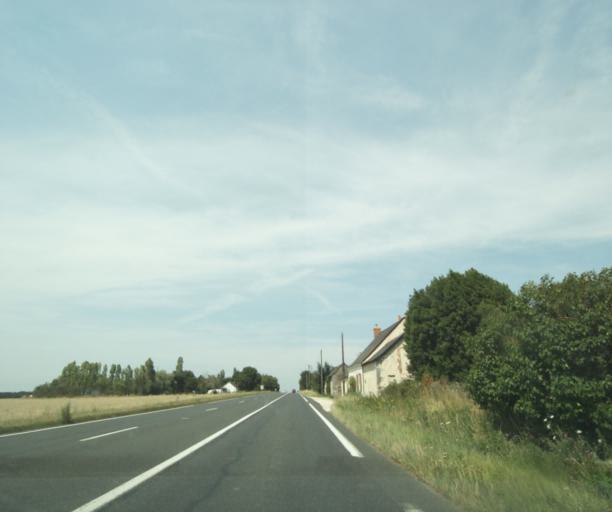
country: FR
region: Centre
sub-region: Departement d'Indre-et-Loire
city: Sainte-Maure-de-Touraine
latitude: 47.1712
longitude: 0.6541
